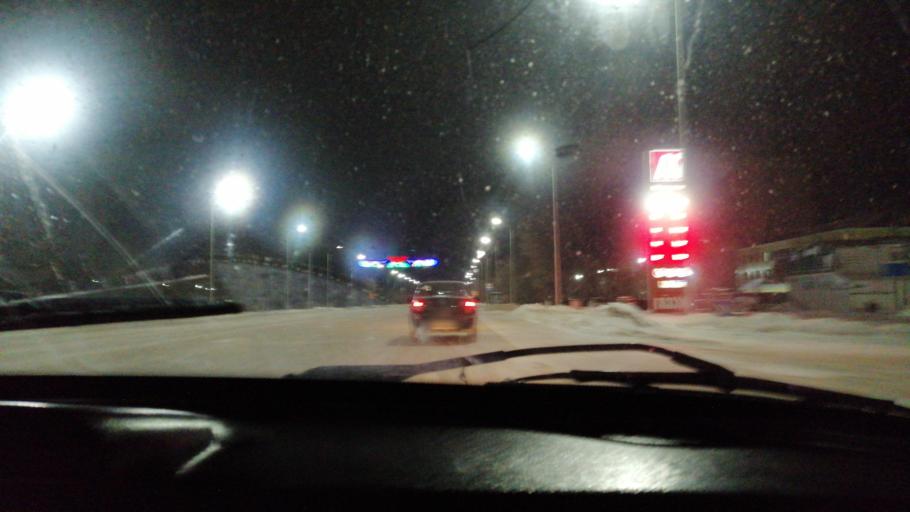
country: KZ
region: Aqtoebe
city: Aqtobe
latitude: 50.2966
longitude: 57.1880
